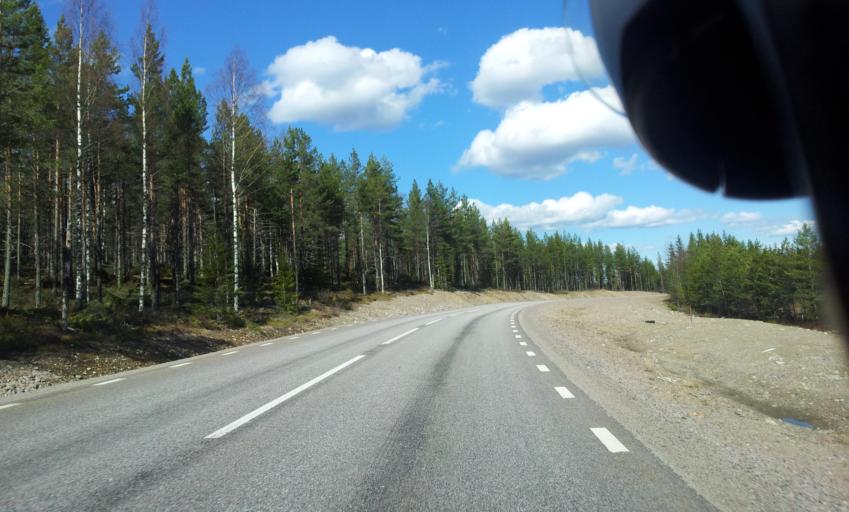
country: SE
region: Gaevleborg
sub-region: Bollnas Kommun
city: Vittsjo
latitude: 61.1249
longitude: 15.8660
